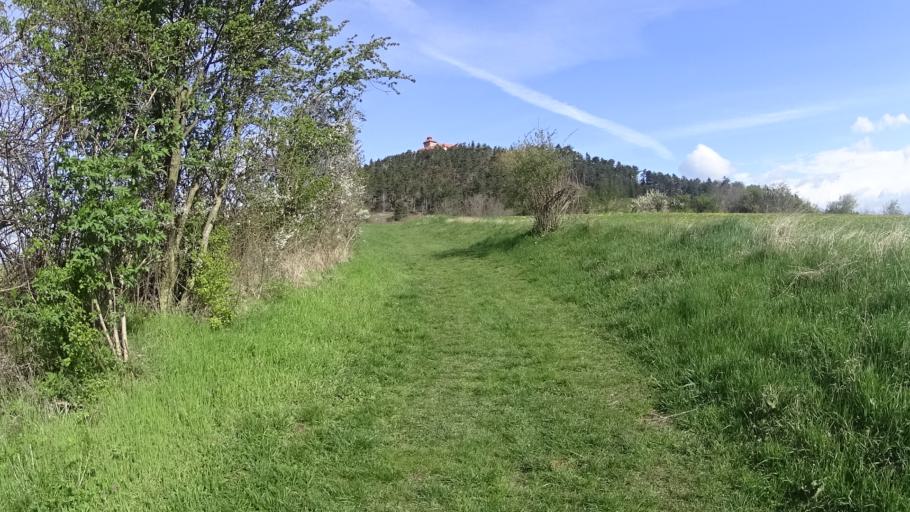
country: DE
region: Thuringia
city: Apfelstadt
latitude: 50.8541
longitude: 10.8784
